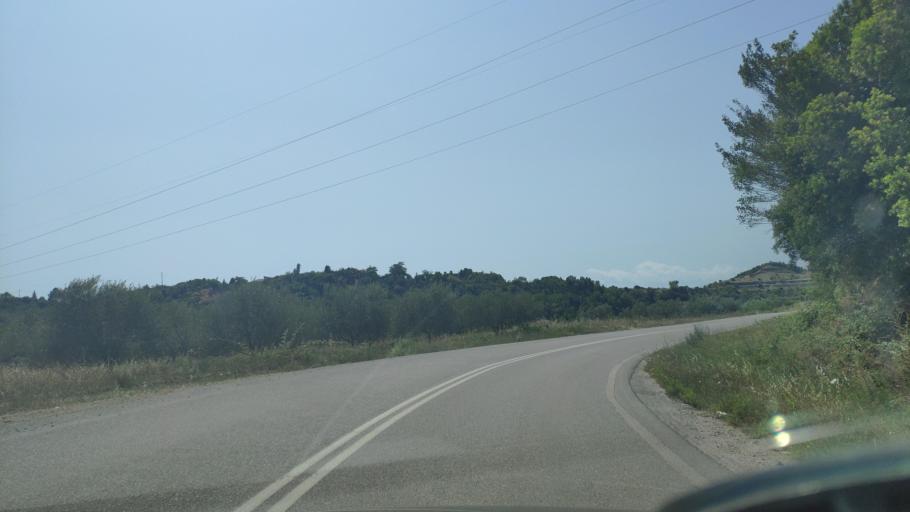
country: GR
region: Epirus
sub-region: Nomos Artas
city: Ano Kalentini
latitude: 39.2123
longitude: 21.1230
